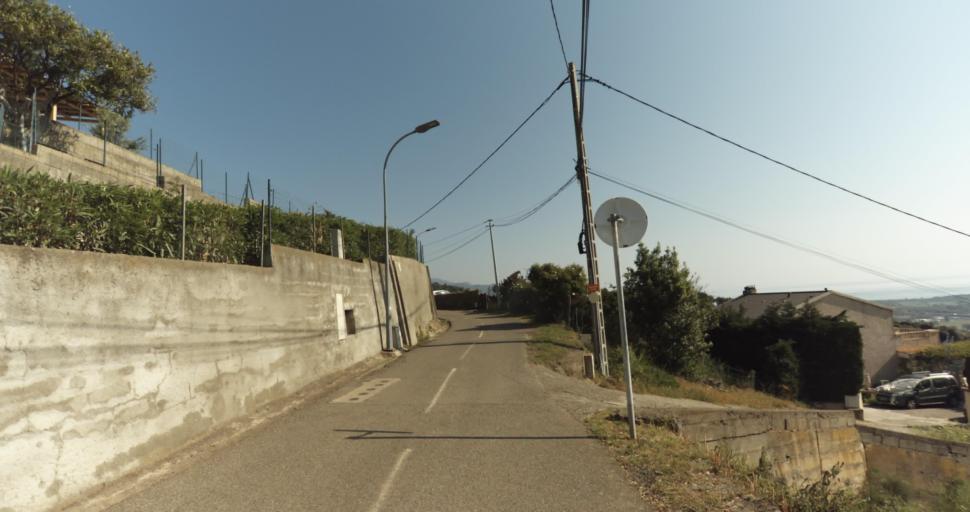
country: FR
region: Corsica
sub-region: Departement de la Haute-Corse
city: Biguglia
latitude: 42.6296
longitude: 9.4186
